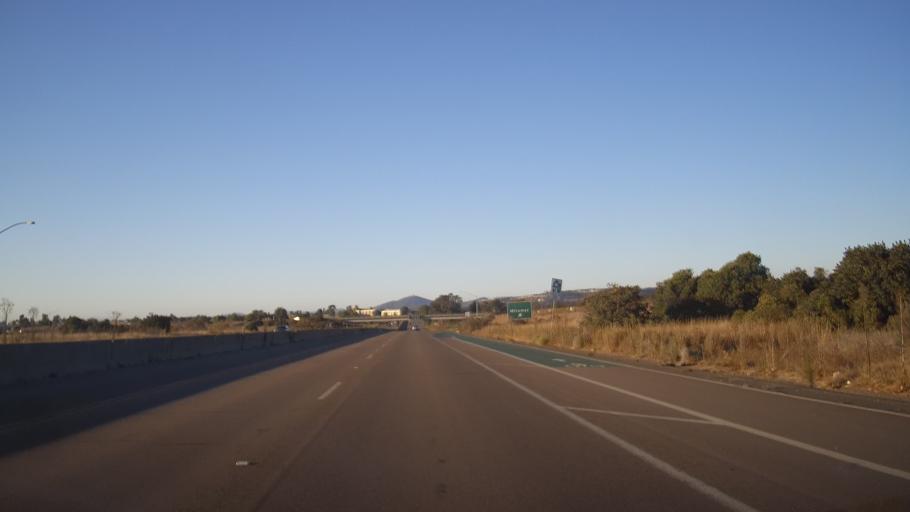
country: US
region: California
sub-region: San Diego County
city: Poway
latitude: 32.8762
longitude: -117.1165
